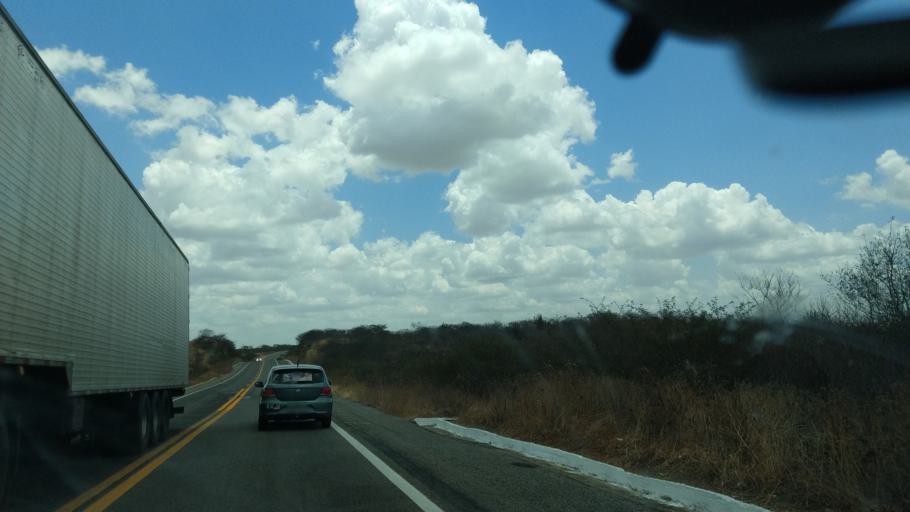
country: BR
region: Rio Grande do Norte
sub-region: Cerro Cora
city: Cerro Cora
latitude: -6.2045
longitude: -36.2786
